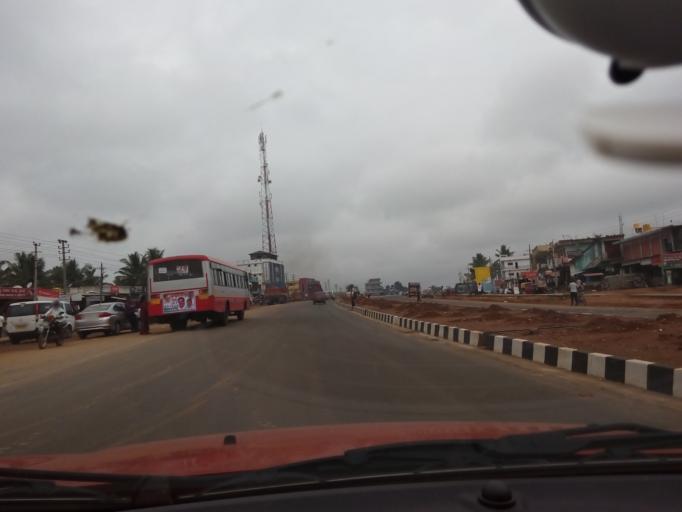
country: IN
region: Karnataka
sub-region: Hassan
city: Shravanabelagola
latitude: 12.9519
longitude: 76.5742
